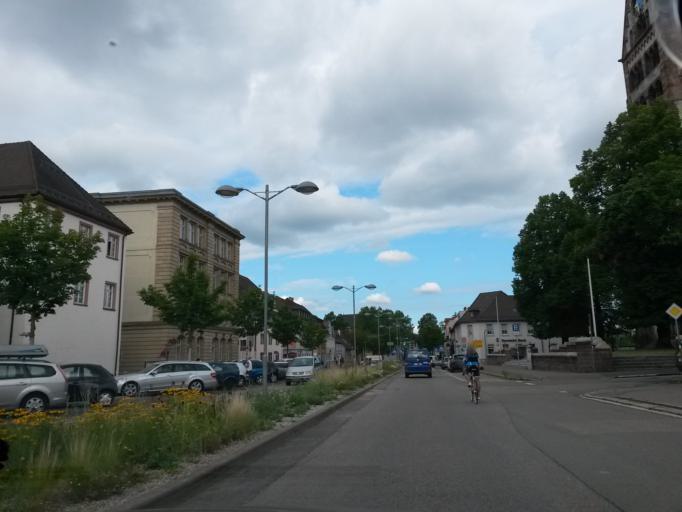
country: DE
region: Baden-Wuerttemberg
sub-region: Karlsruhe Region
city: Ettlingen
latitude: 48.9427
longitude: 8.4106
